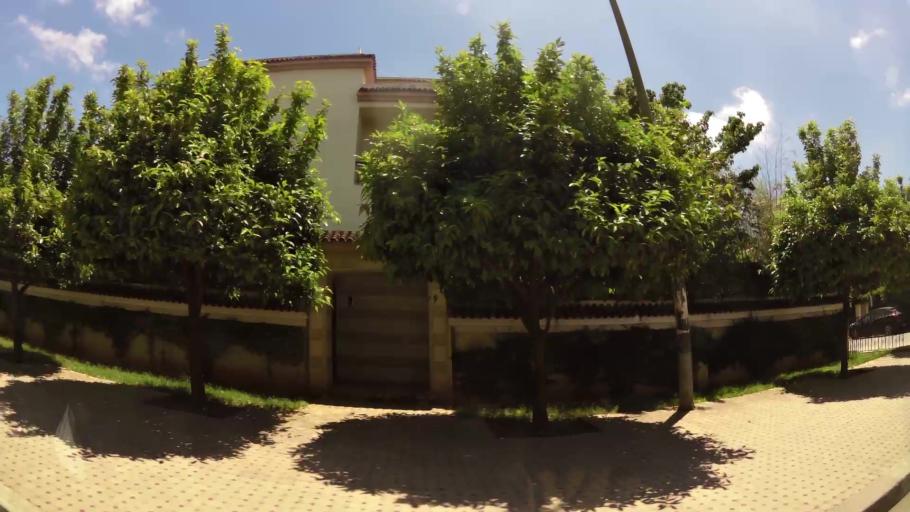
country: MA
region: Fes-Boulemane
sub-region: Fes
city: Fes
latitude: 34.0062
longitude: -4.9901
